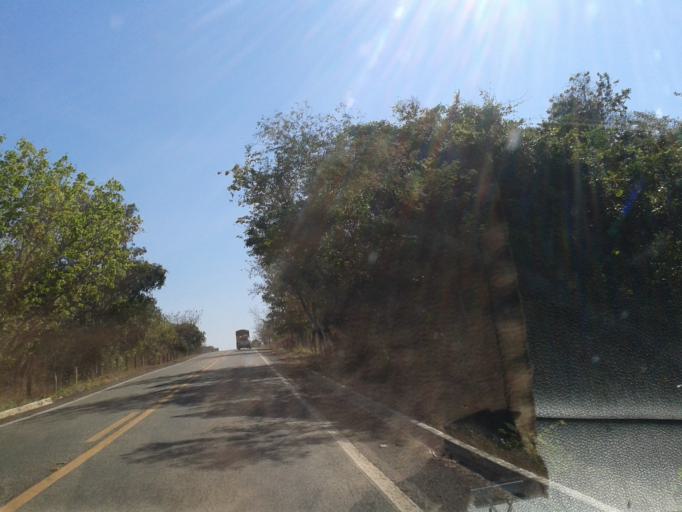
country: BR
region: Goias
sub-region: Crixas
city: Crixas
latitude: -14.0634
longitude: -50.3314
